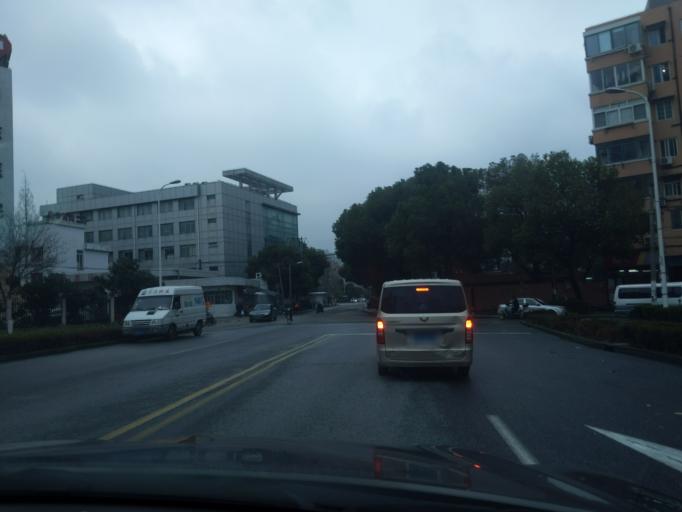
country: CN
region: Shanghai Shi
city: Huamu
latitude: 31.1883
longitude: 121.5254
